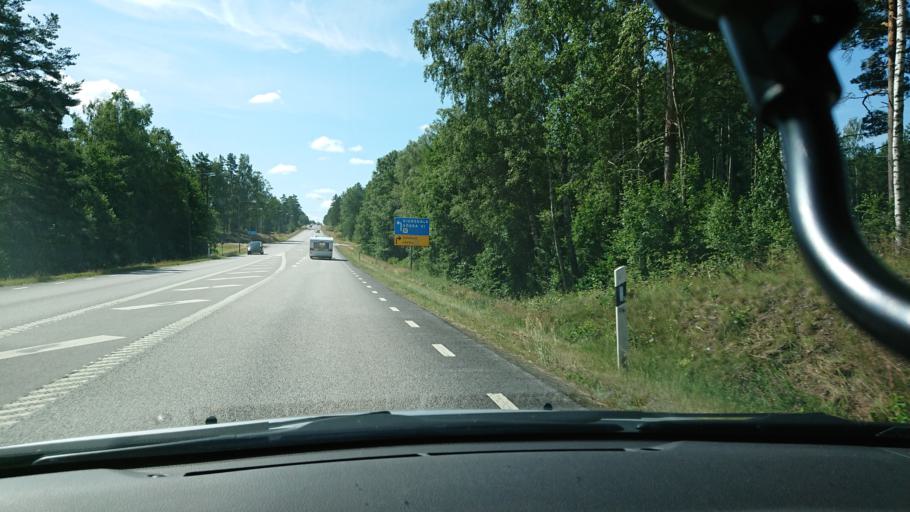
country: SE
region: Kalmar
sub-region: Vimmerby Kommun
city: Sodra Vi
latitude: 57.7565
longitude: 15.7732
